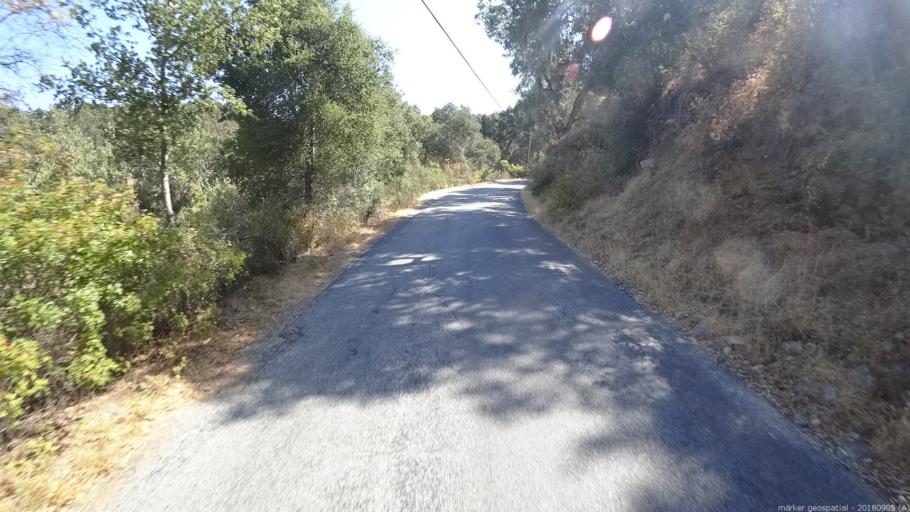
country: US
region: California
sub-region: Monterey County
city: Carmel Valley Village
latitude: 36.3960
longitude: -121.6434
